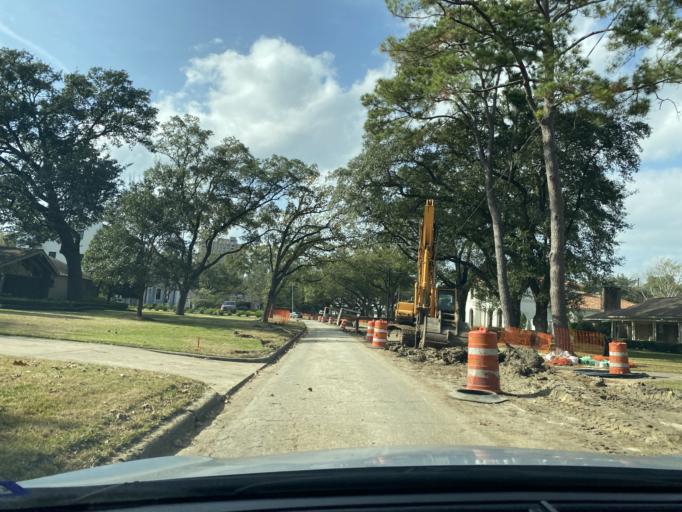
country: US
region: Texas
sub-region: Harris County
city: Hunters Creek Village
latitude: 29.7630
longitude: -95.4738
